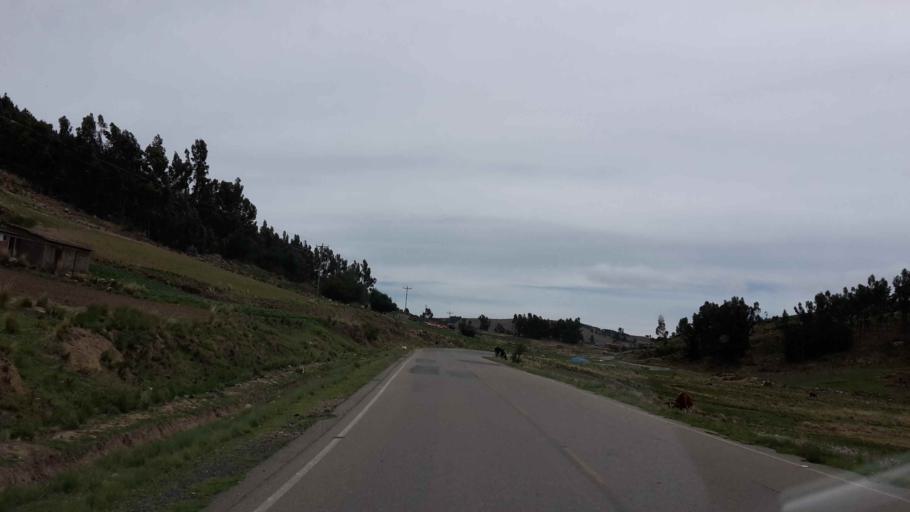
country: BO
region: Cochabamba
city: Arani
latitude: -17.4828
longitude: -65.6042
